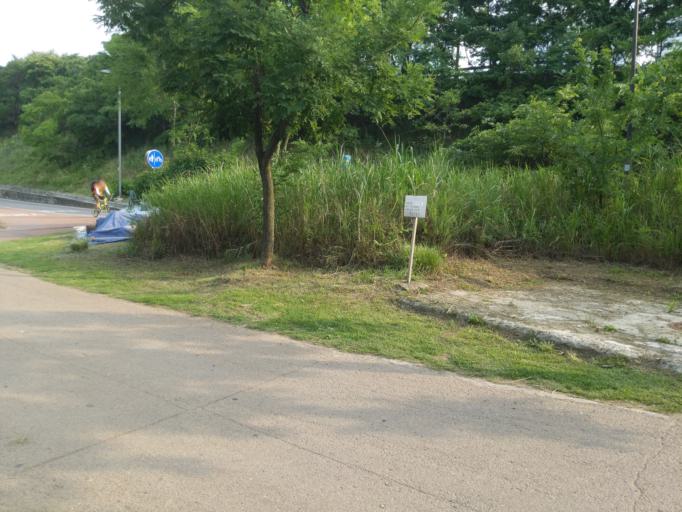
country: KR
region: Gyeonggi-do
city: Kwangmyong
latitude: 37.5361
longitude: 126.9066
